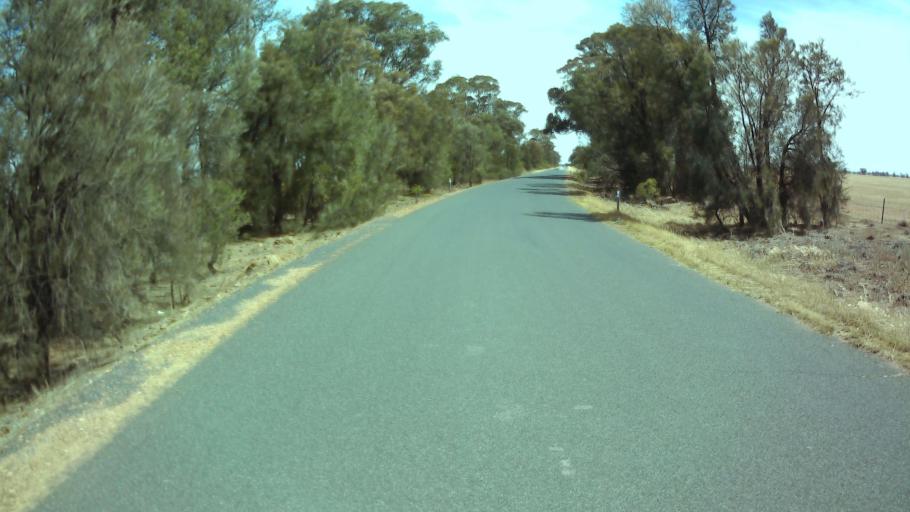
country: AU
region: New South Wales
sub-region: Weddin
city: Grenfell
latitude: -33.9461
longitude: 147.7788
